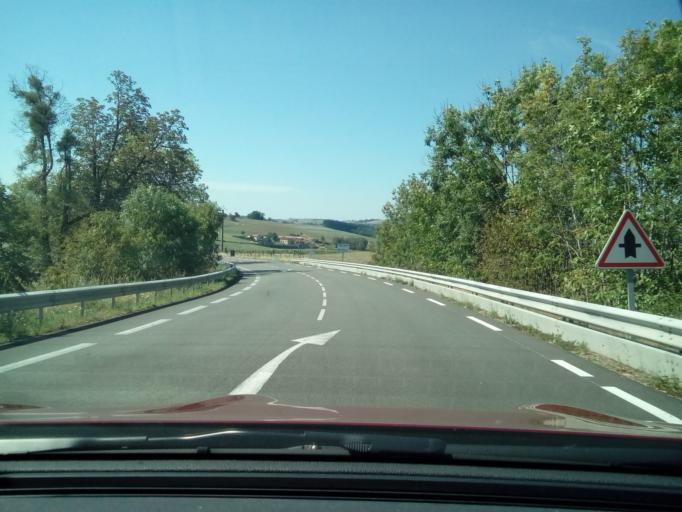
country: FR
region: Rhone-Alpes
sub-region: Departement du Rhone
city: Cublize
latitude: 45.9800
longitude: 4.3828
